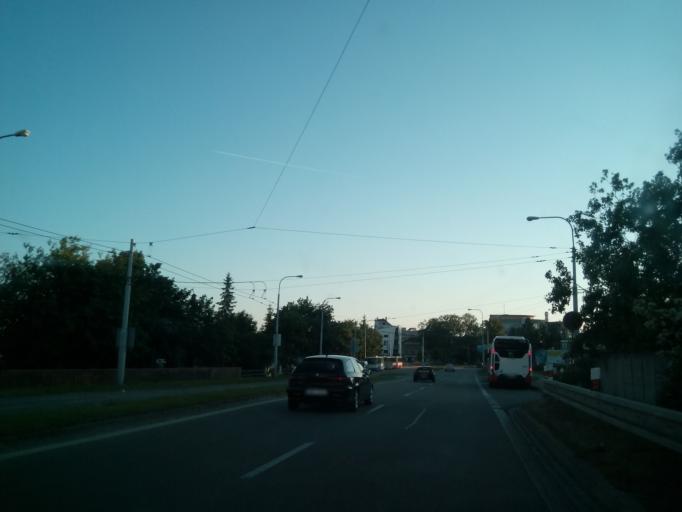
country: CZ
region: South Moravian
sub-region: Mesto Brno
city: Brno
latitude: 49.2020
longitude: 16.6428
